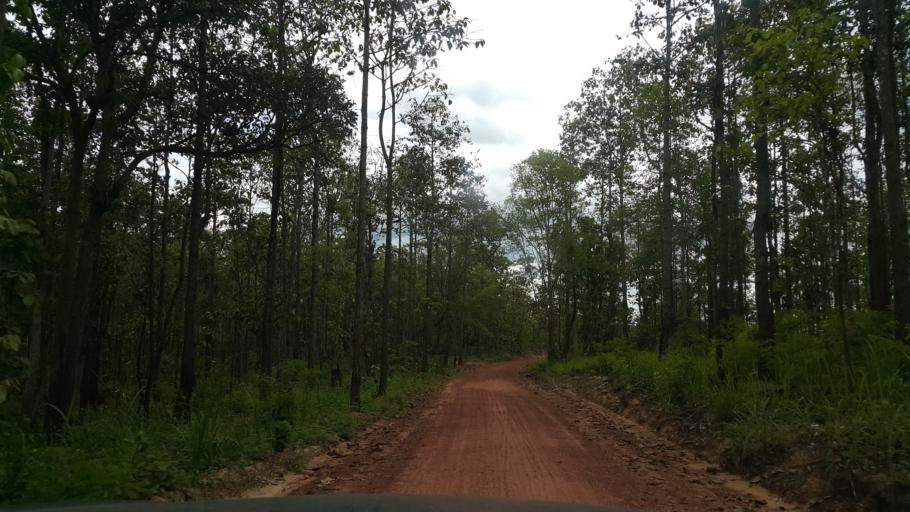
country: TH
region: Chiang Mai
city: Mae Taeng
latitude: 19.2235
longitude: 98.9953
